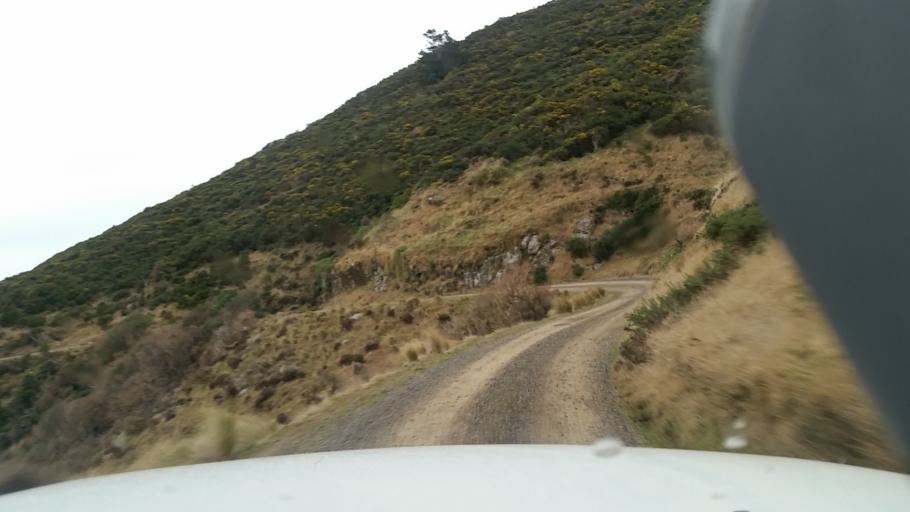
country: NZ
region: Canterbury
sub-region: Christchurch City
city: Christchurch
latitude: -43.8539
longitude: 172.8858
